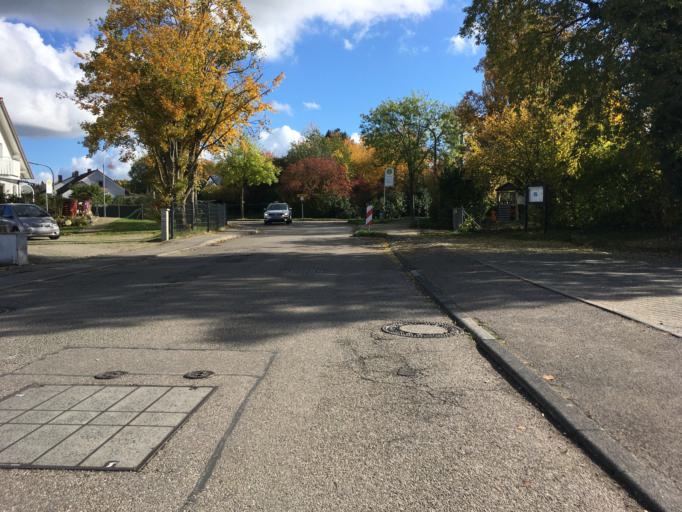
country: DE
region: Baden-Wuerttemberg
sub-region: Regierungsbezirk Stuttgart
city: Pfedelbach
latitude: 49.1782
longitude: 9.5084
